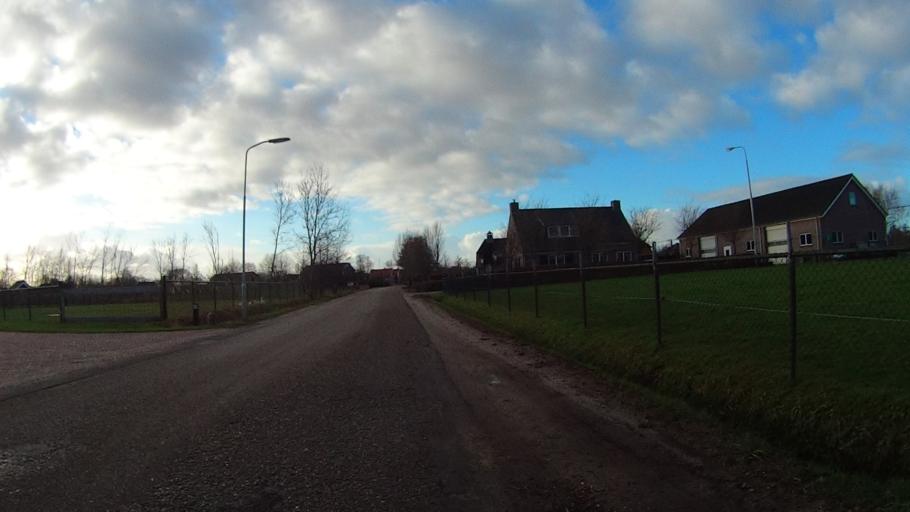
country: NL
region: Gelderland
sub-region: Gemeente Barneveld
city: Zwartebroek
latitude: 52.1866
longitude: 5.4856
